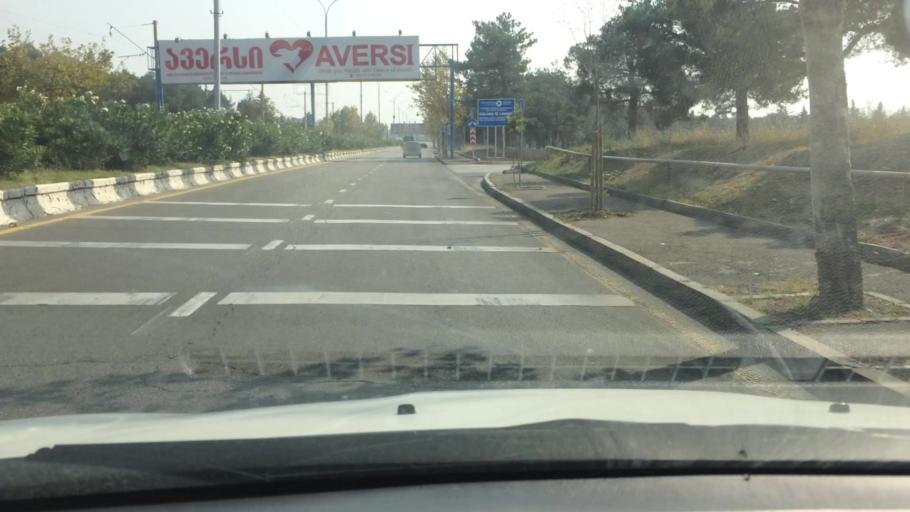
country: GE
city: Didi Lilo
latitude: 41.6774
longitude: 44.9597
